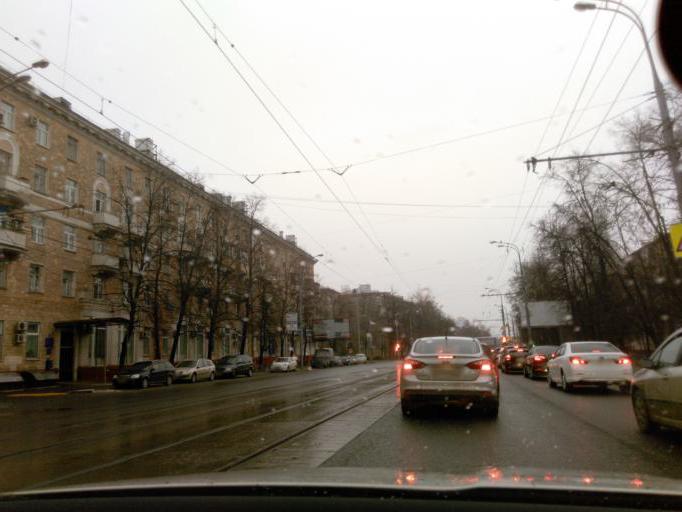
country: RU
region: Moscow
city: Pokrovskoye-Streshnevo
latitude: 55.8277
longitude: 37.4524
